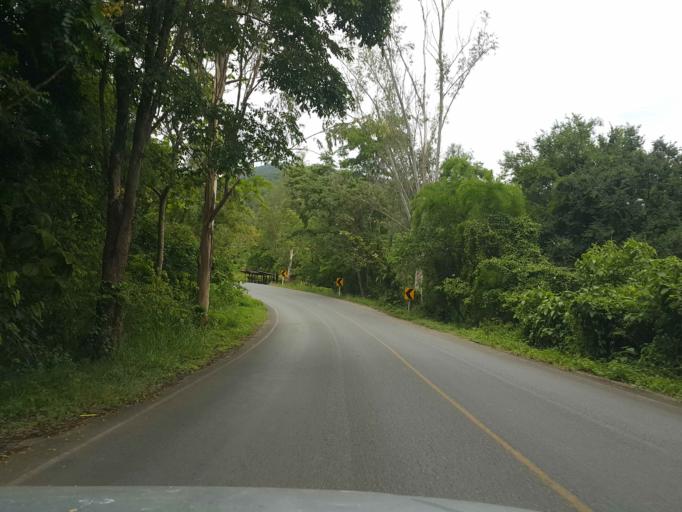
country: TH
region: Lampang
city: Thoen
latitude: 17.5994
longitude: 99.3310
